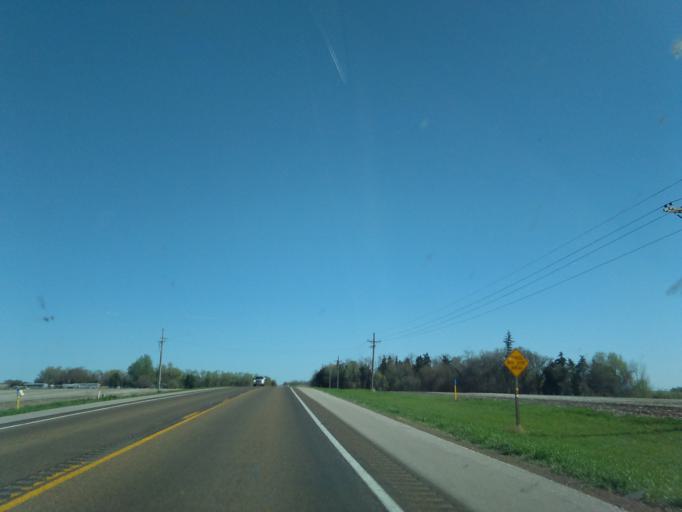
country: US
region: Nebraska
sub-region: Dodge County
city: Fremont
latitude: 41.3539
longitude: -96.5021
